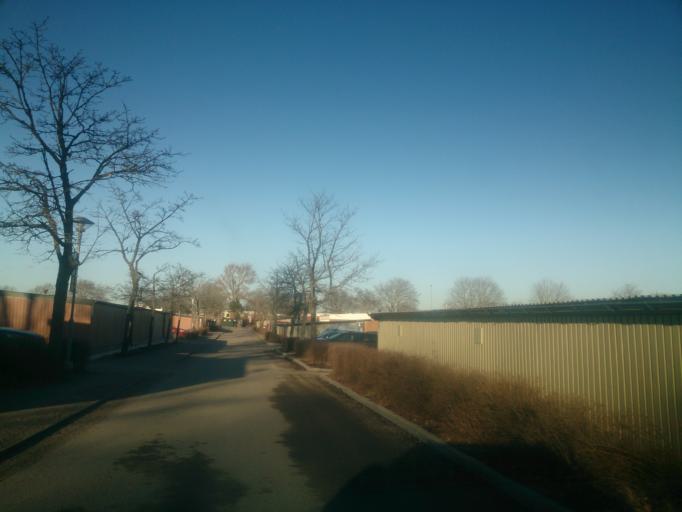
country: SE
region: OEstergoetland
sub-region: Norrkopings Kommun
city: Norrkoping
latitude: 58.5613
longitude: 16.2145
